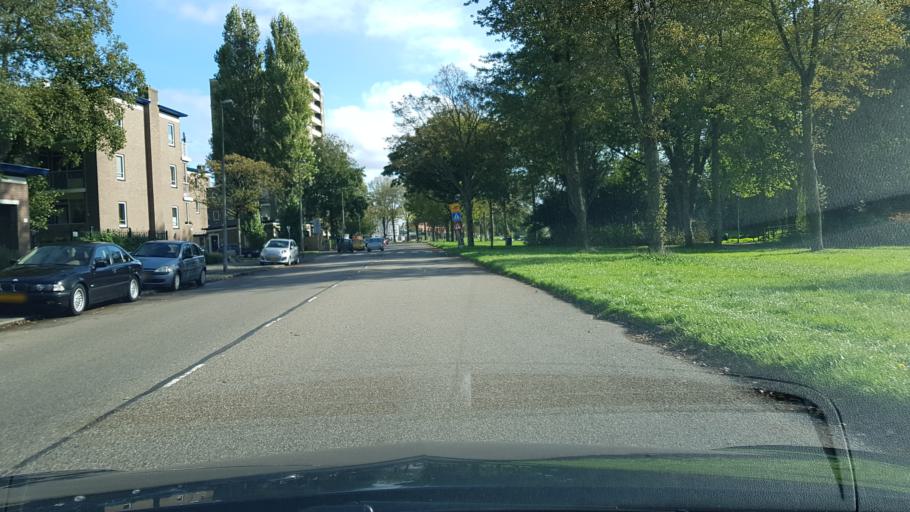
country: NL
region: North Holland
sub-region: Gemeente Bloemendaal
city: Bloemendaal
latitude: 52.4144
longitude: 4.6422
